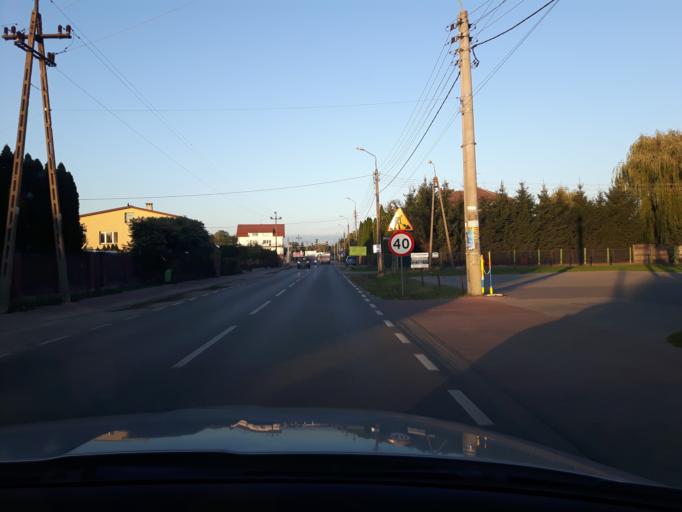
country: PL
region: Masovian Voivodeship
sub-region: Powiat wolominski
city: Kobylka
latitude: 52.3364
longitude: 21.1781
